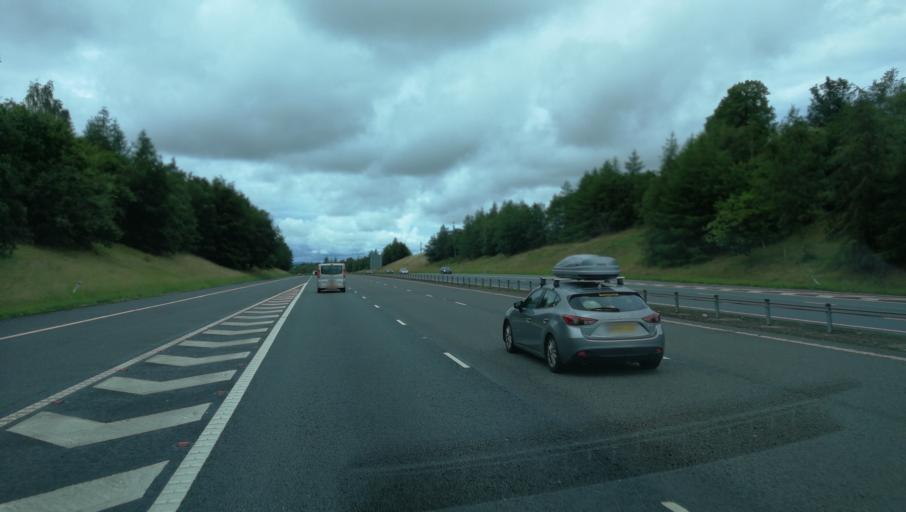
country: GB
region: Scotland
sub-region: Dumfries and Galloway
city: Lockerbie
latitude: 55.1358
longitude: -3.3701
